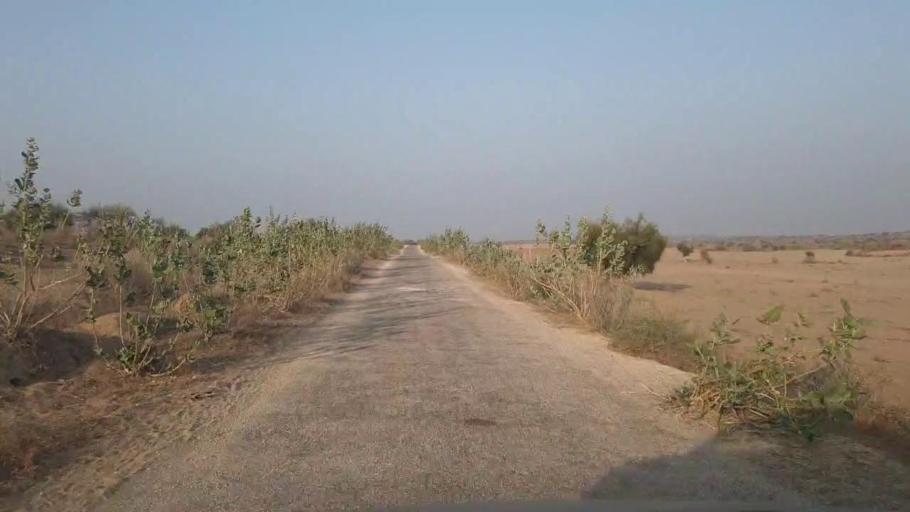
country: PK
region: Sindh
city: Umarkot
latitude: 25.2432
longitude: 69.8961
